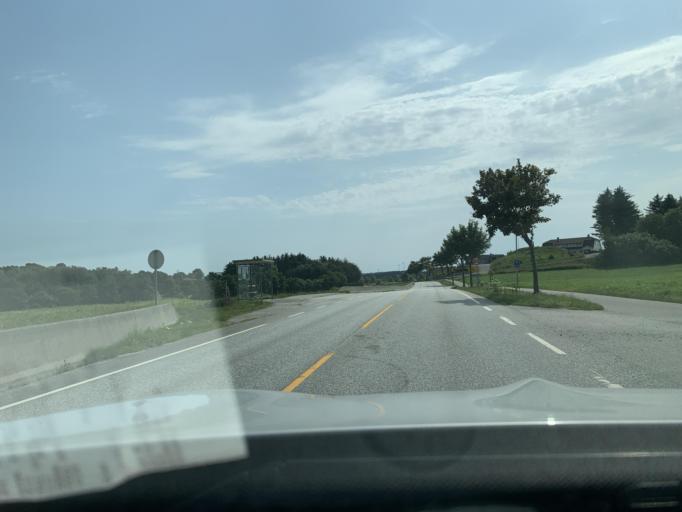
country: NO
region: Rogaland
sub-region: Klepp
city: Kleppe
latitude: 58.7632
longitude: 5.6249
